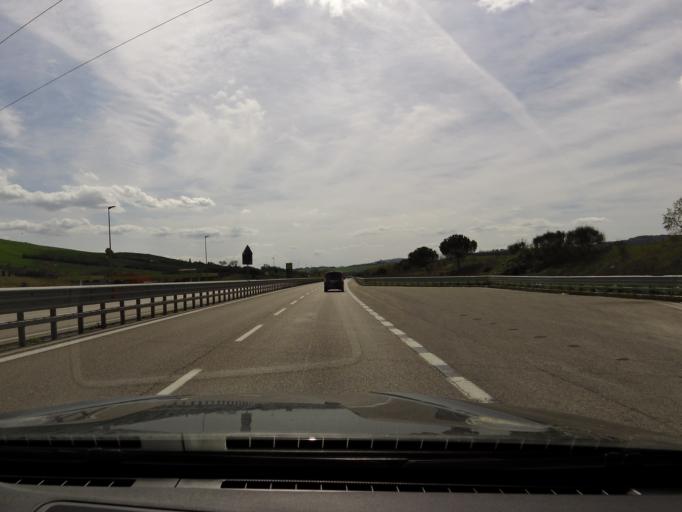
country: IT
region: The Marches
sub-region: Provincia di Ancona
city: San Biagio
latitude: 43.5531
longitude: 13.5173
